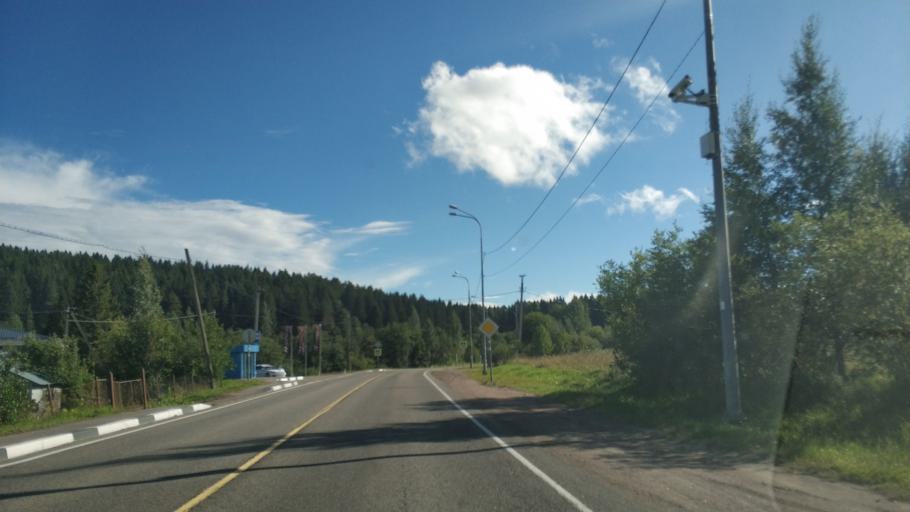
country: RU
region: Republic of Karelia
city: Sortavala
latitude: 61.6602
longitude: 30.6565
